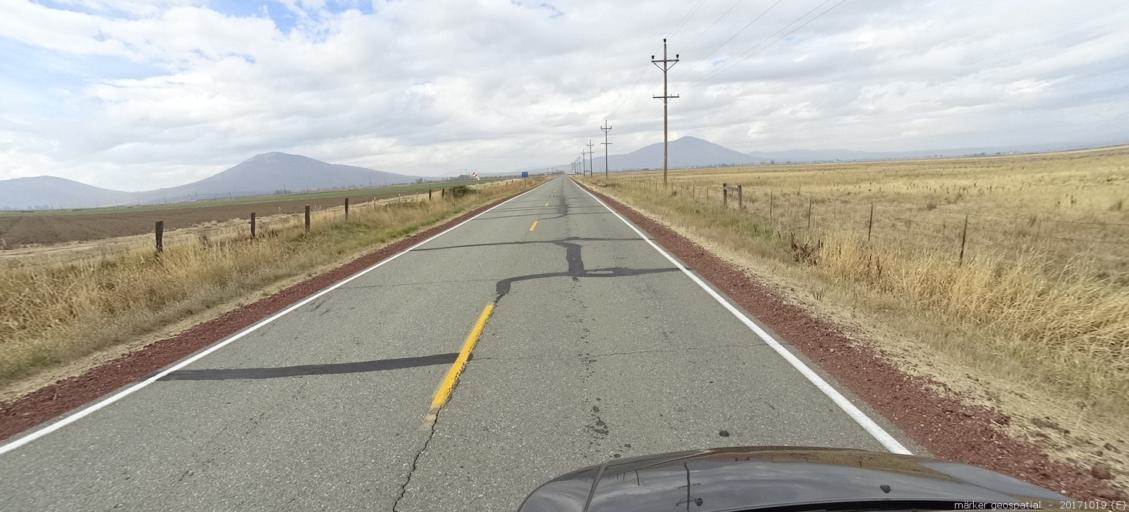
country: US
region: California
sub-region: Shasta County
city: Burney
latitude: 41.0509
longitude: -121.4206
